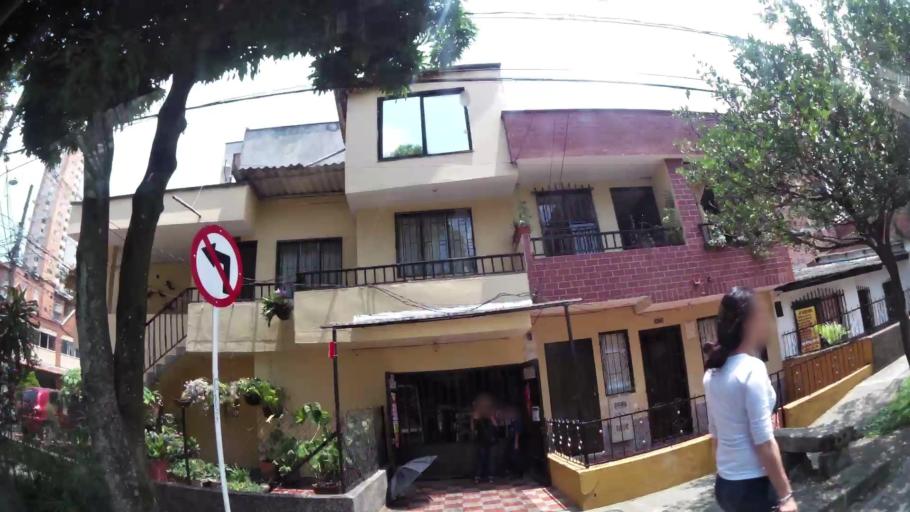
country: CO
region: Antioquia
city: Sabaneta
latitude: 6.1669
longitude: -75.6171
